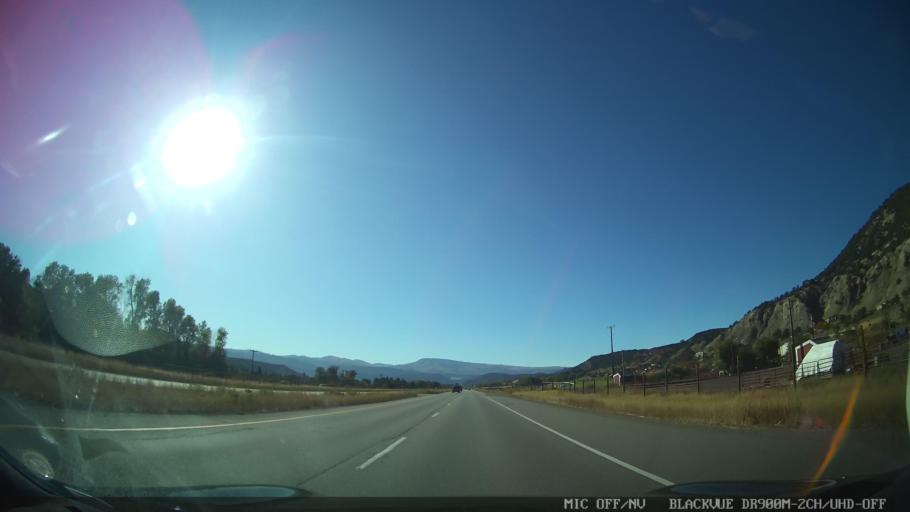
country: US
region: Colorado
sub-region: Eagle County
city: El Jebel
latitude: 39.4055
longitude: -107.1383
